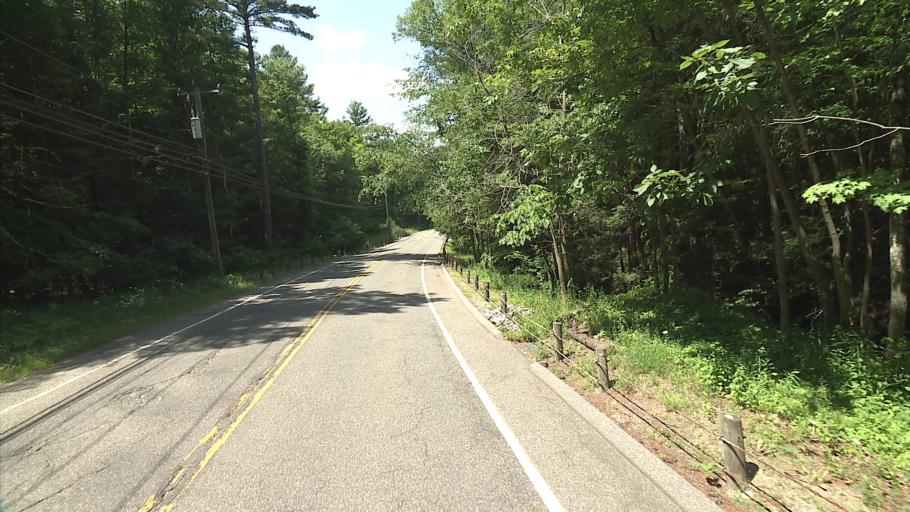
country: US
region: Connecticut
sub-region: Litchfield County
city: Canaan
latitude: 41.8723
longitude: -73.3351
